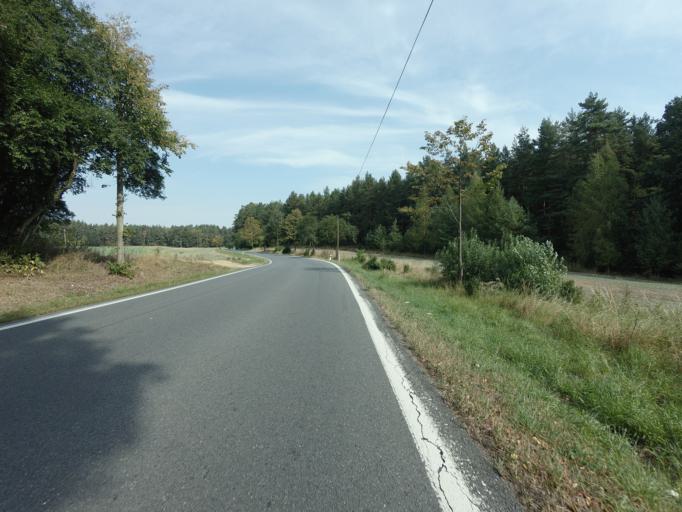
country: CZ
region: Central Bohemia
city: Petrovice
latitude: 49.5296
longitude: 14.3544
